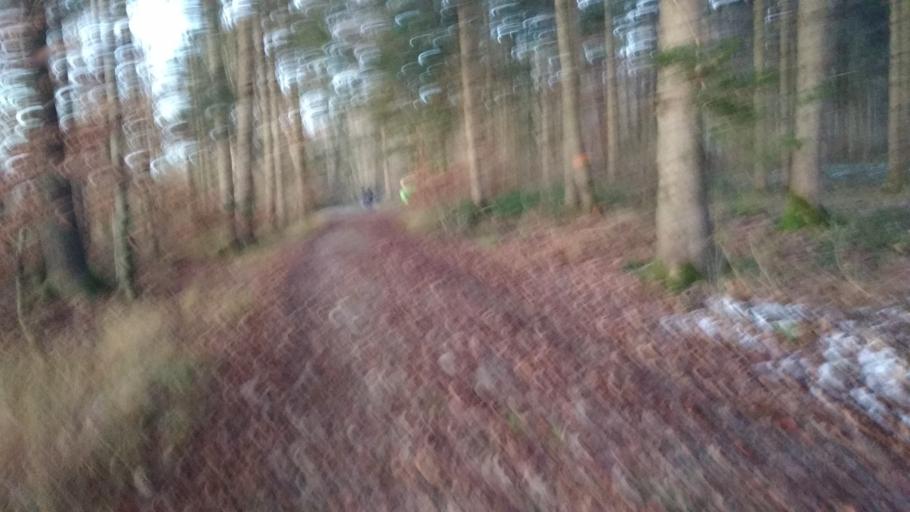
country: DE
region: Bavaria
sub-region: Upper Bavaria
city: Vaterstetten
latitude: 48.0759
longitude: 11.7848
